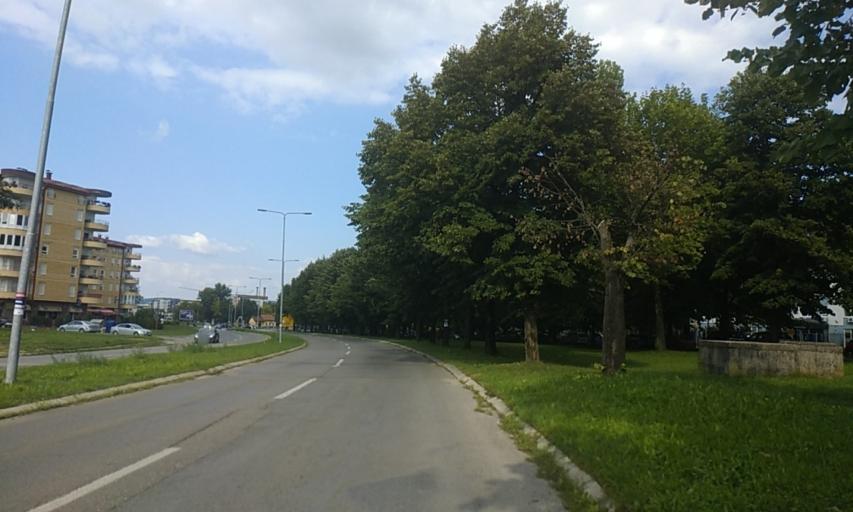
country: BA
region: Republika Srpska
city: Starcevica
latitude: 44.7643
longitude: 17.2076
